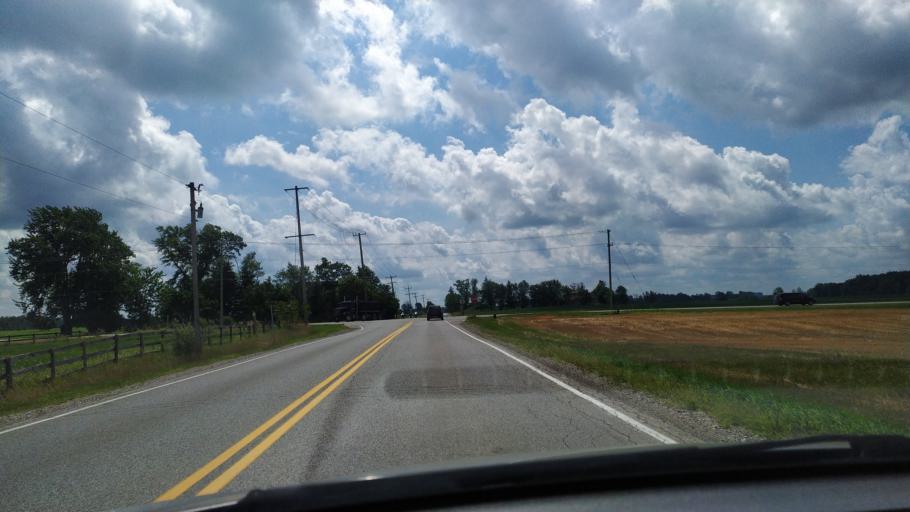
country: CA
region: Ontario
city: London
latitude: 43.0431
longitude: -81.3232
